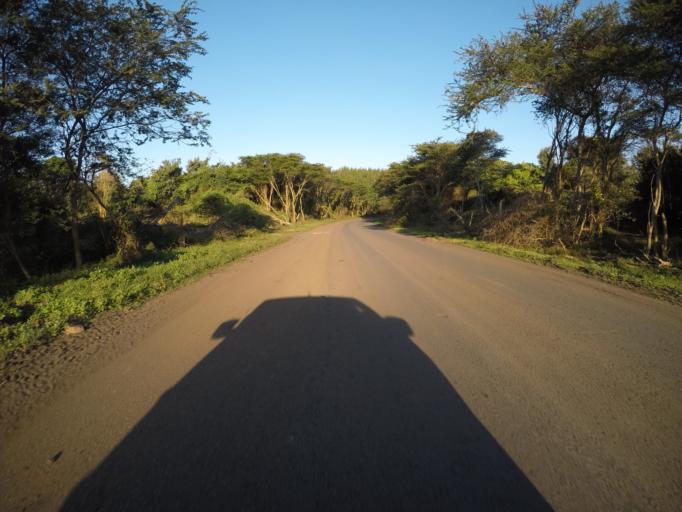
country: ZA
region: KwaZulu-Natal
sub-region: uThungulu District Municipality
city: KwaMbonambi
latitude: -28.6930
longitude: 32.2099
